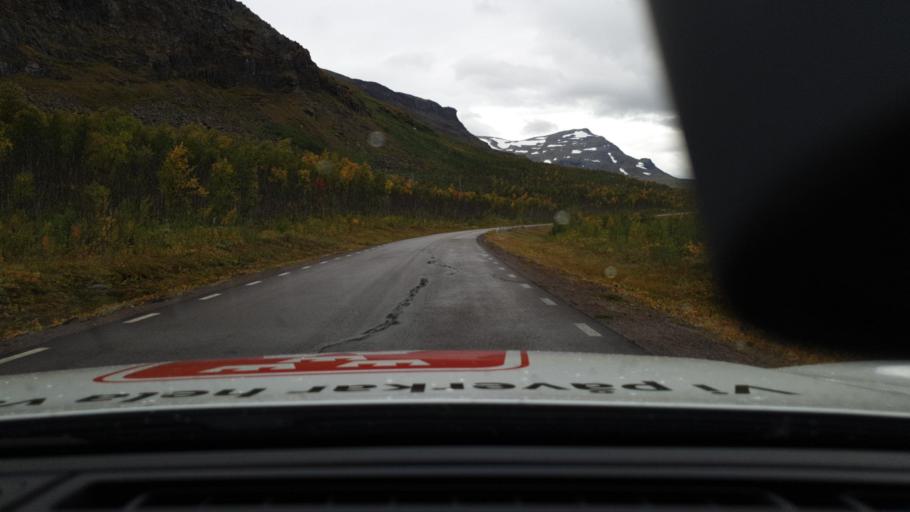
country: NO
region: Troms
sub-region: Bardu
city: Setermoen
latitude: 68.4277
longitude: 18.3917
